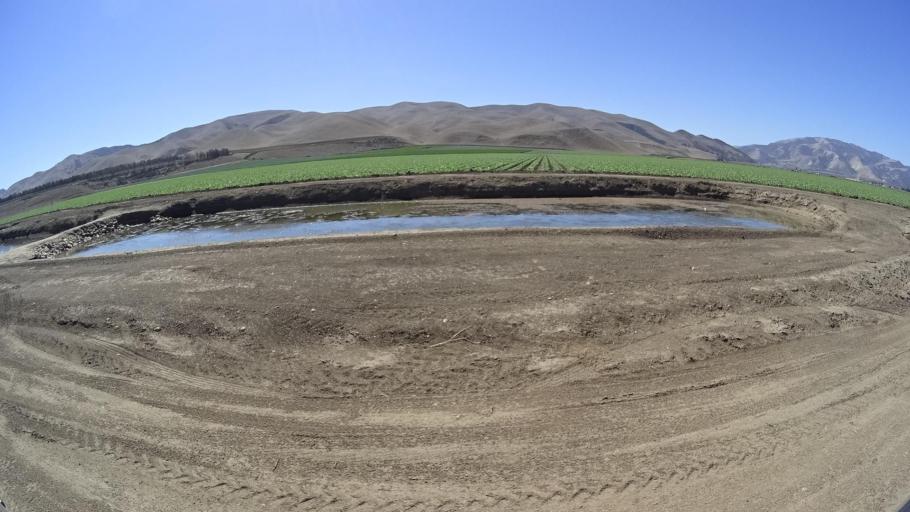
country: US
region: California
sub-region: Monterey County
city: Greenfield
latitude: 36.2844
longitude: -121.2410
